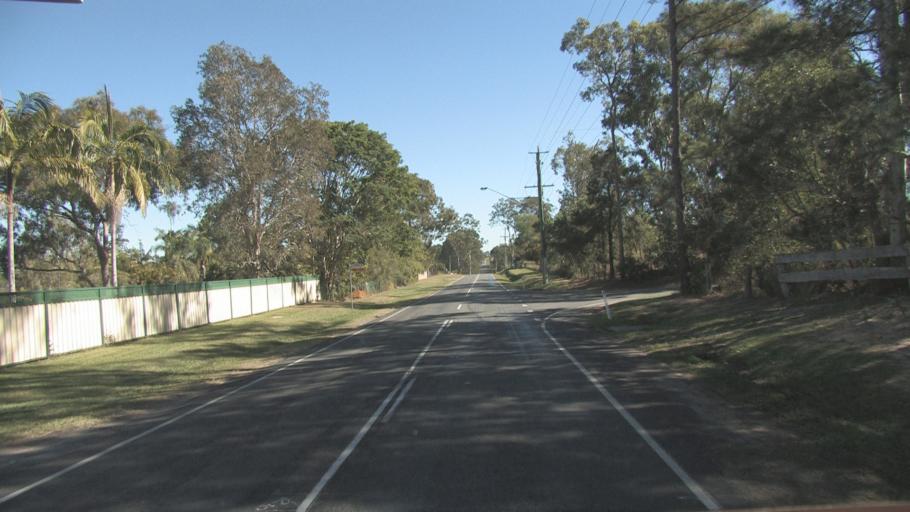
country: AU
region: Queensland
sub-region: Logan
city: Park Ridge South
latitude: -27.7173
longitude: 153.0461
